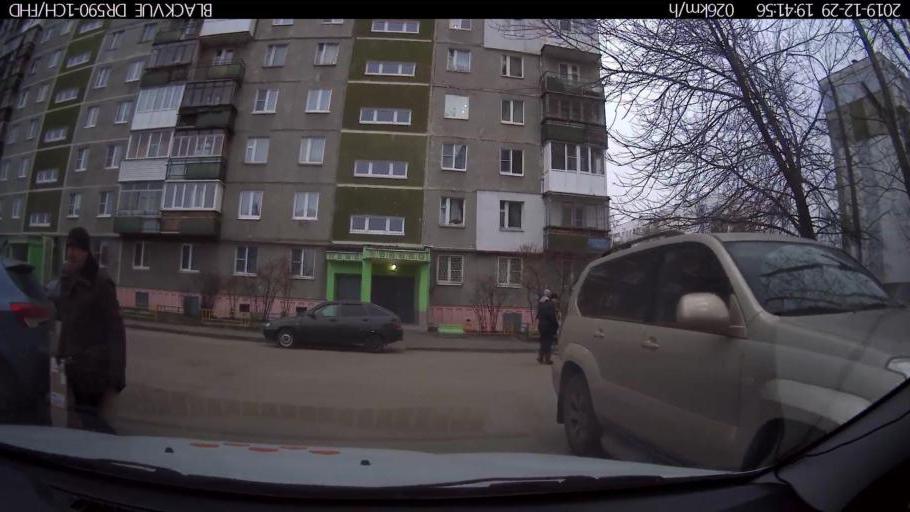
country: RU
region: Nizjnij Novgorod
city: Neklyudovo
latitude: 56.3489
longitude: 43.8549
